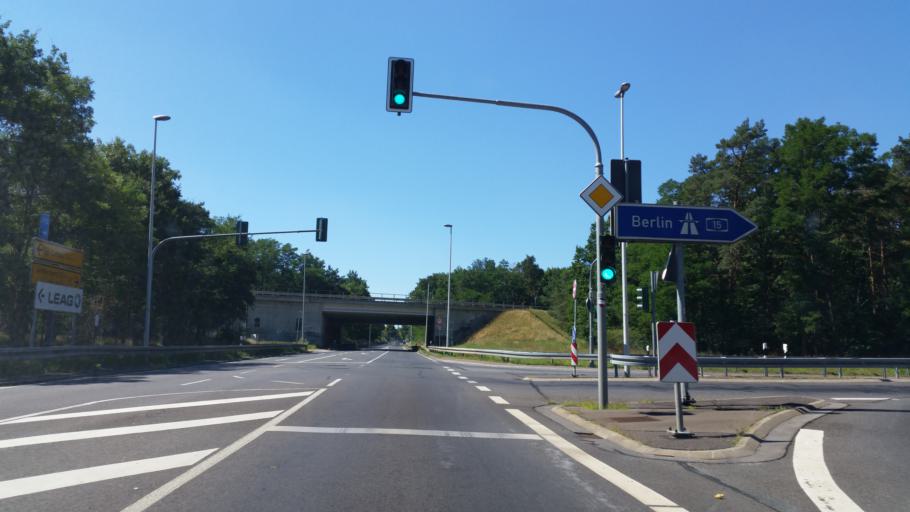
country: DE
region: Brandenburg
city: Cottbus
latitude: 51.7251
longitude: 14.3023
